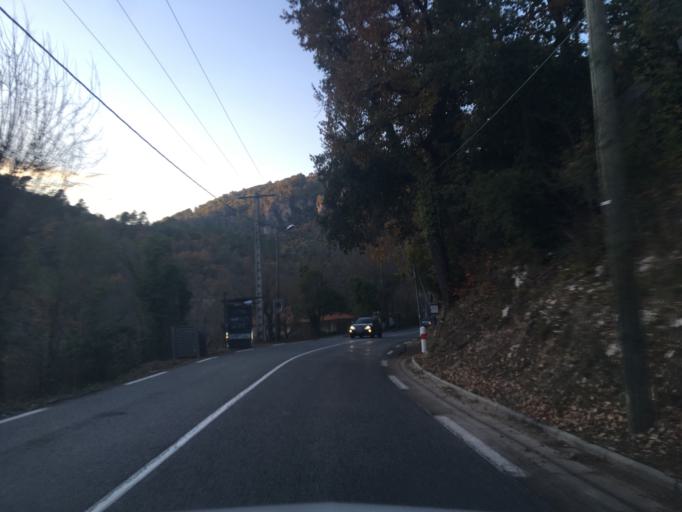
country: FR
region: Provence-Alpes-Cote d'Azur
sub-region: Departement des Alpes-Maritimes
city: Le Tignet
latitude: 43.6273
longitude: 6.8196
